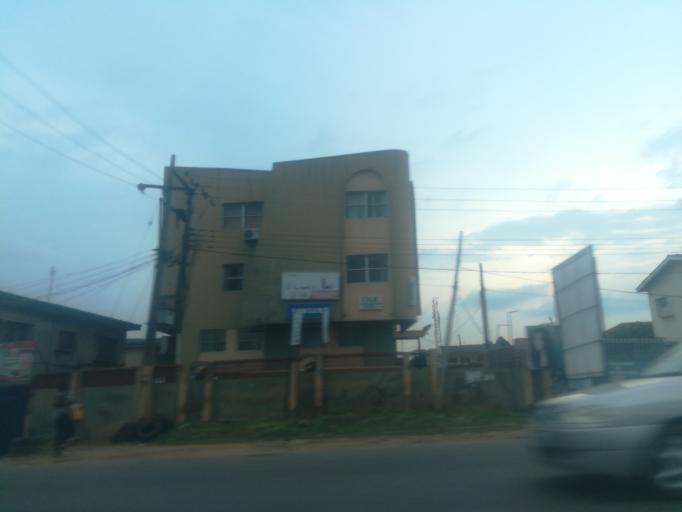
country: NG
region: Oyo
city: Ibadan
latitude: 7.4280
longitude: 3.9105
